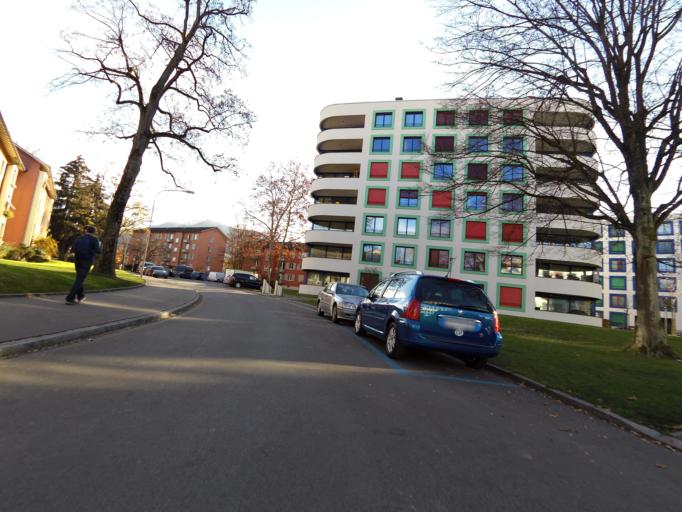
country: CH
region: Zurich
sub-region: Bezirk Zuerich
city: Zuerich (Kreis 9) / Albisrieden
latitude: 47.3776
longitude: 8.4882
